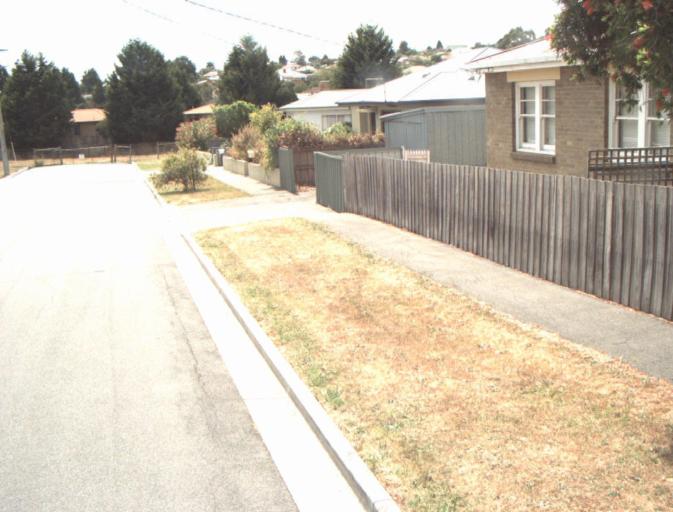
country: AU
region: Tasmania
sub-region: Launceston
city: Newnham
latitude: -41.3992
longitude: 147.1312
